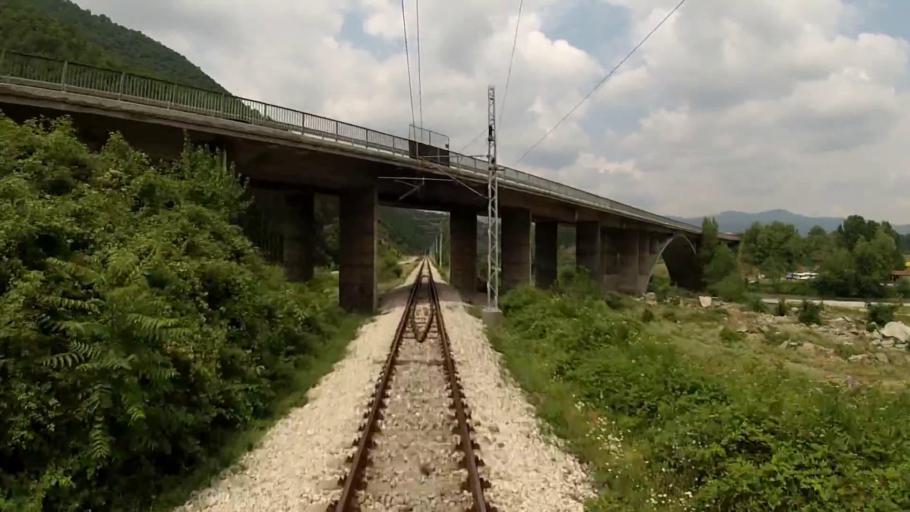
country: BG
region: Blagoevgrad
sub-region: Obshtina Kresna
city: Stara Kresna
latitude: 41.8414
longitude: 23.1509
